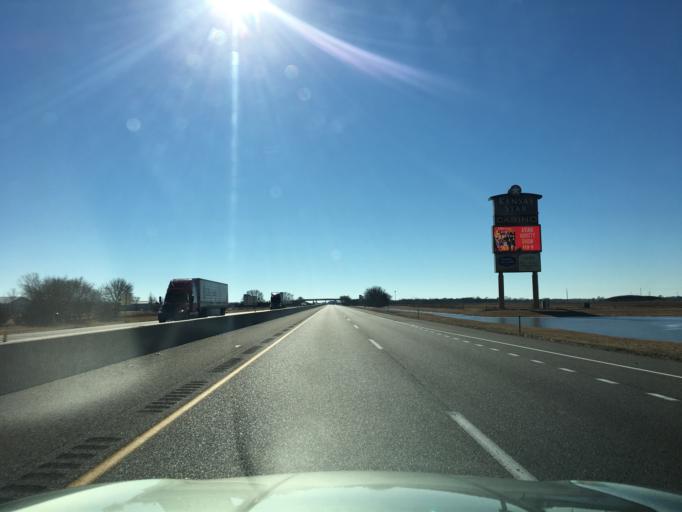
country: US
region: Kansas
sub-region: Sumner County
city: Mulvane
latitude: 37.4708
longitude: -97.3228
